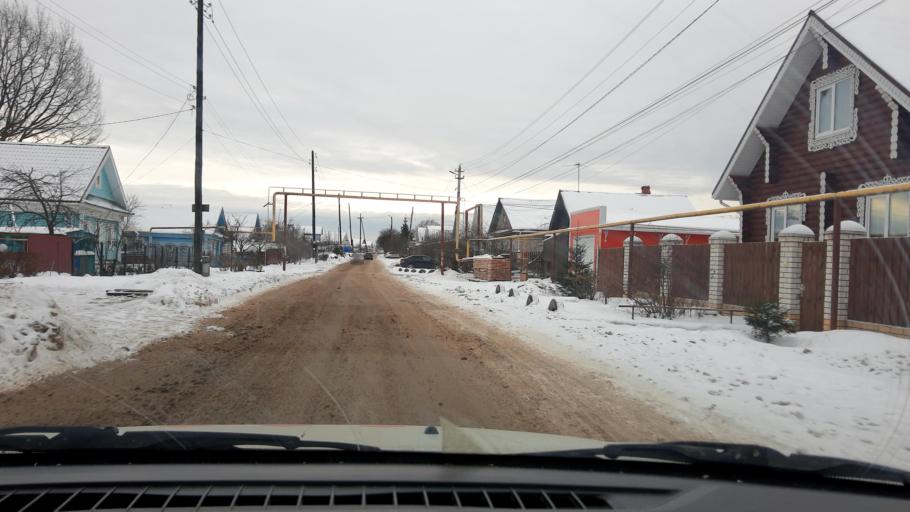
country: RU
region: Nizjnij Novgorod
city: Gorodets
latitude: 56.6628
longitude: 43.4794
